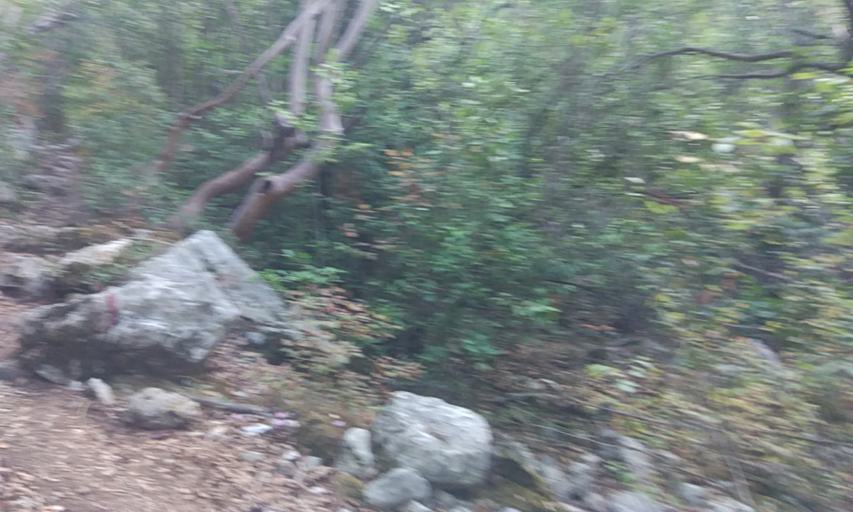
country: TR
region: Antalya
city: Tekirova
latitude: 36.3828
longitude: 30.4747
